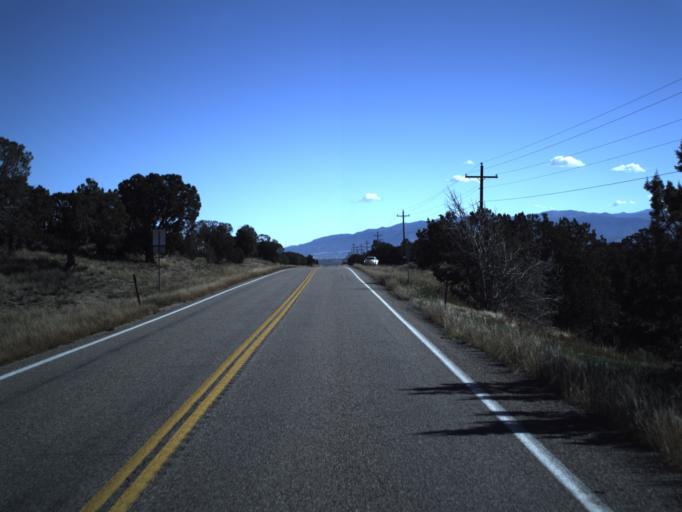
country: US
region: Utah
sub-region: Iron County
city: Cedar City
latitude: 37.6406
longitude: -113.2563
